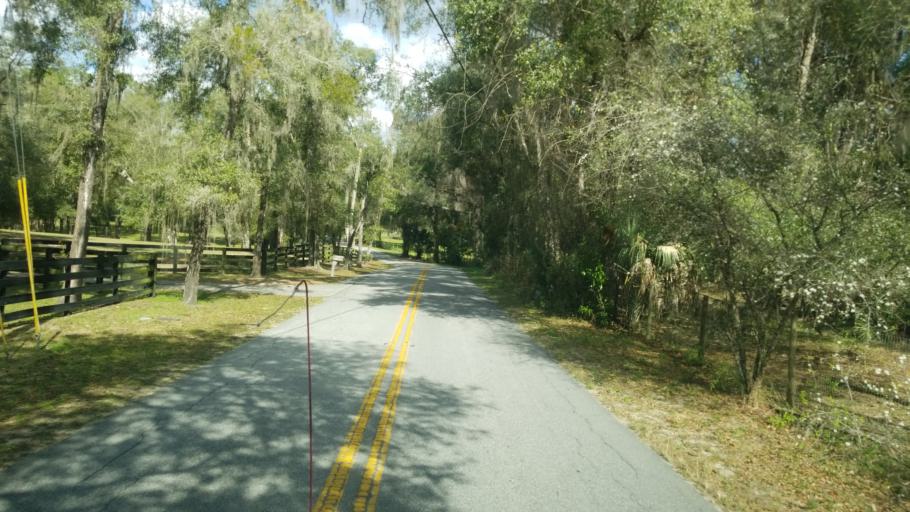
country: US
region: Florida
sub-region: Citrus County
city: Floral City
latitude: 28.7442
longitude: -82.2960
